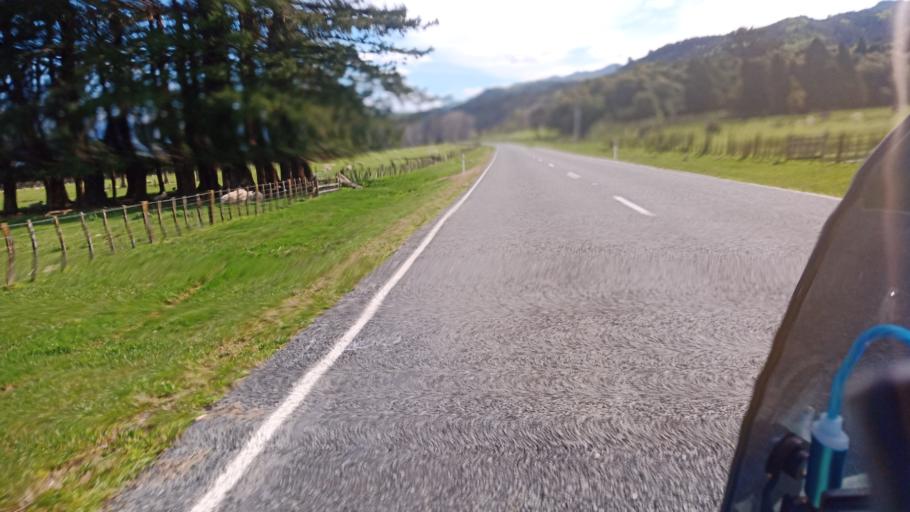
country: NZ
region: Gisborne
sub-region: Gisborne District
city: Gisborne
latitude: -37.8671
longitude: 178.2627
